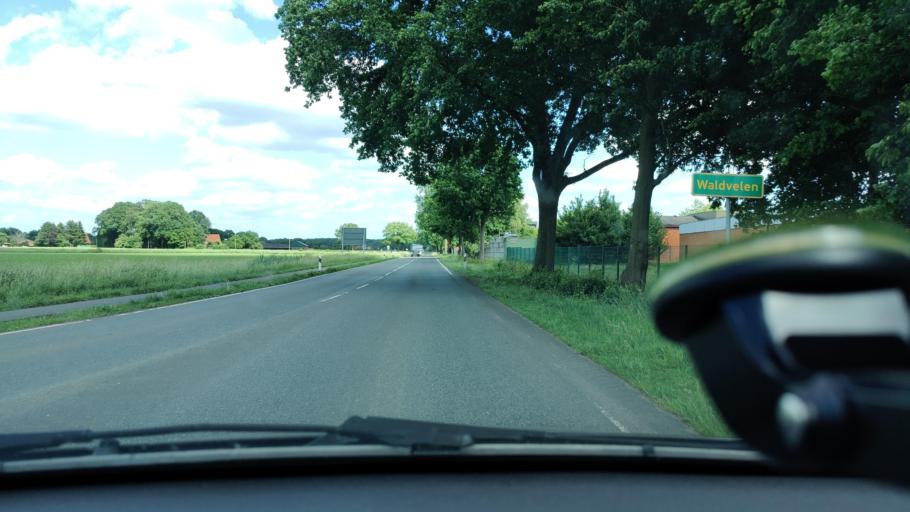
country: DE
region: North Rhine-Westphalia
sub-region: Regierungsbezirk Munster
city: Velen
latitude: 51.8978
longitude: 6.9935
